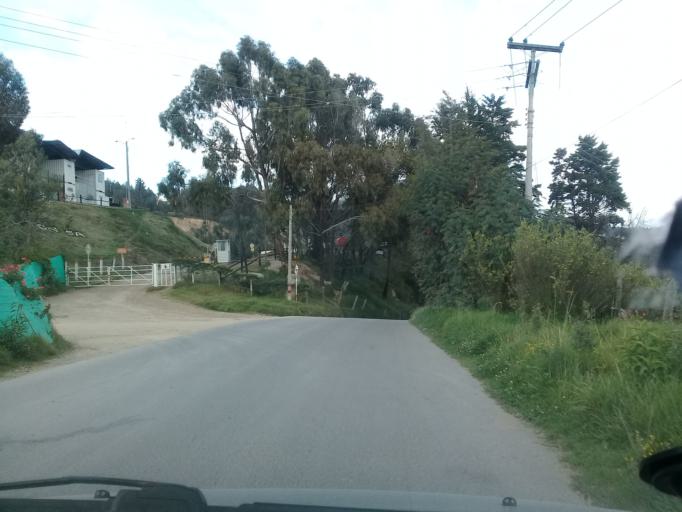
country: CO
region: Cundinamarca
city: El Rosal
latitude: 4.7984
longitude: -74.2137
